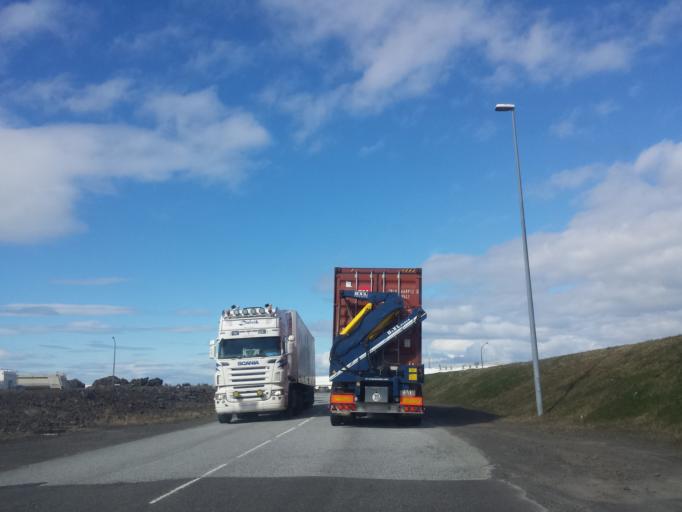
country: IS
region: Capital Region
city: Gardabaer
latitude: 64.0767
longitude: -21.9284
